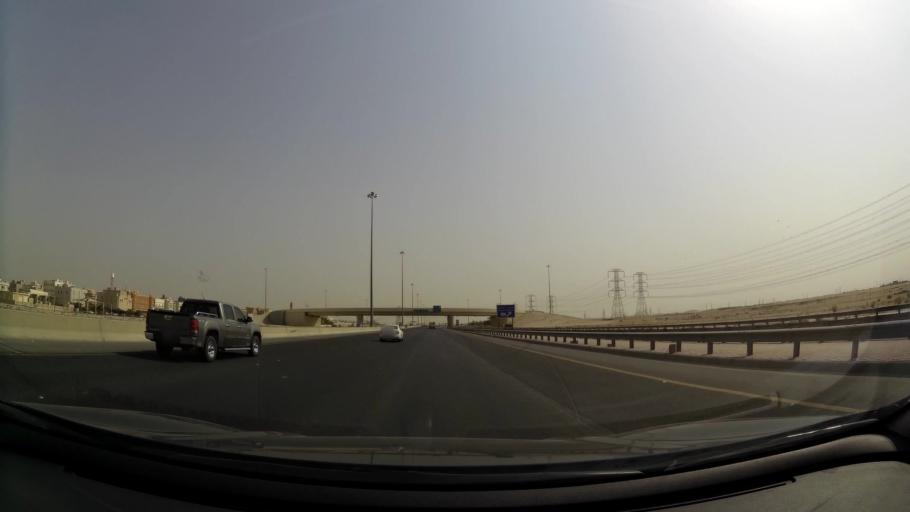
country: KW
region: Muhafazat al Jahra'
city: Al Jahra'
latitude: 29.2986
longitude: 47.7124
